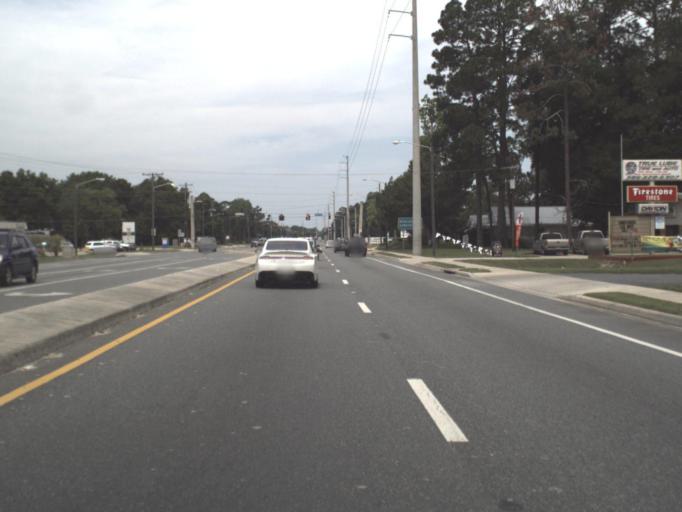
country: US
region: Florida
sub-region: Putnam County
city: Palatka
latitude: 29.6414
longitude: -81.6768
